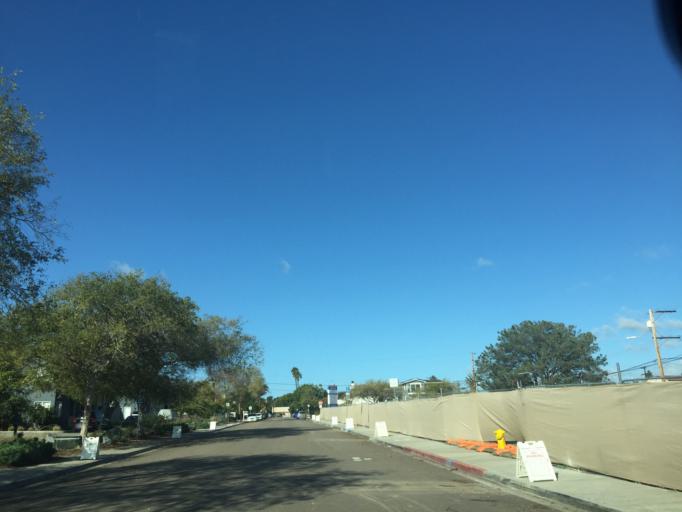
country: US
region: California
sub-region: San Diego County
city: La Jolla
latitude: 32.7919
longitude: -117.2355
